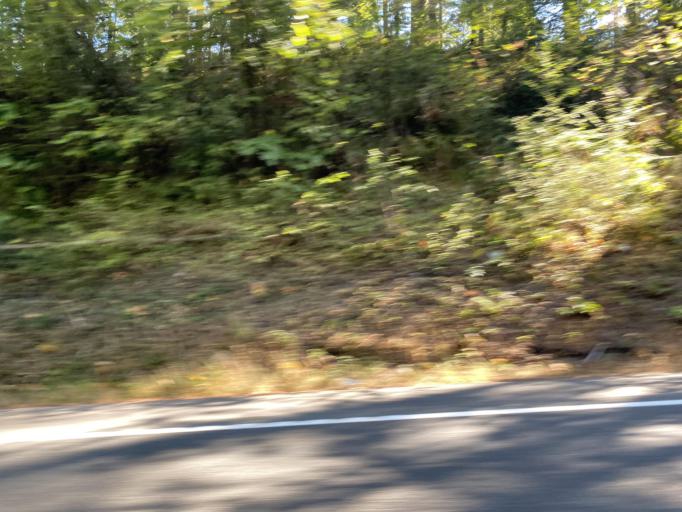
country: US
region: Washington
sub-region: Thurston County
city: Rainier
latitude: 46.9143
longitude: -122.7363
